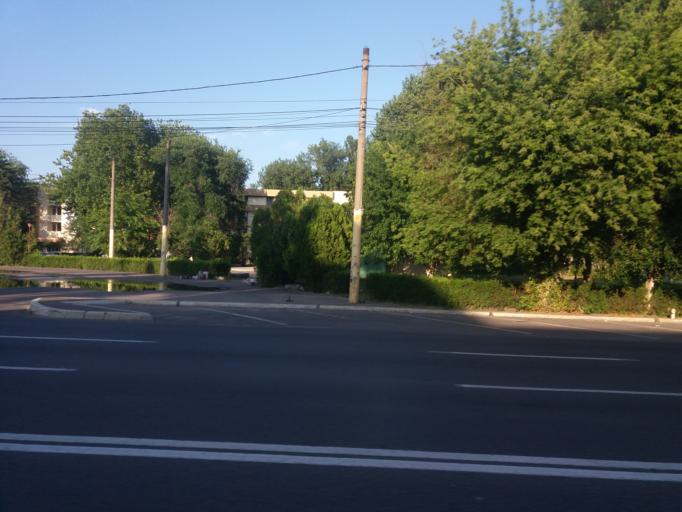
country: RO
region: Constanta
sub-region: Municipiul Constanta
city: Palazu Mare
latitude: 44.2498
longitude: 28.6192
